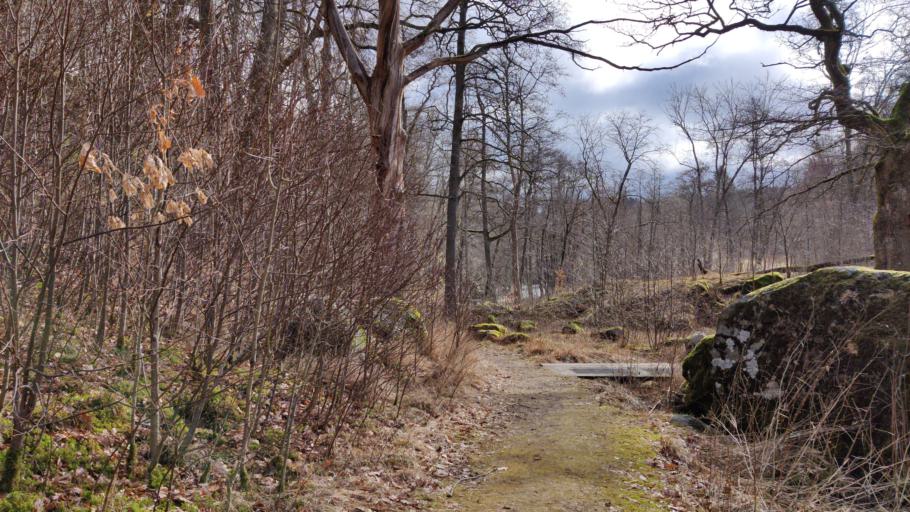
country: SE
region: Vaestra Goetaland
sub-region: Uddevalla Kommun
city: Uddevalla
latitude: 58.3477
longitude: 11.9593
